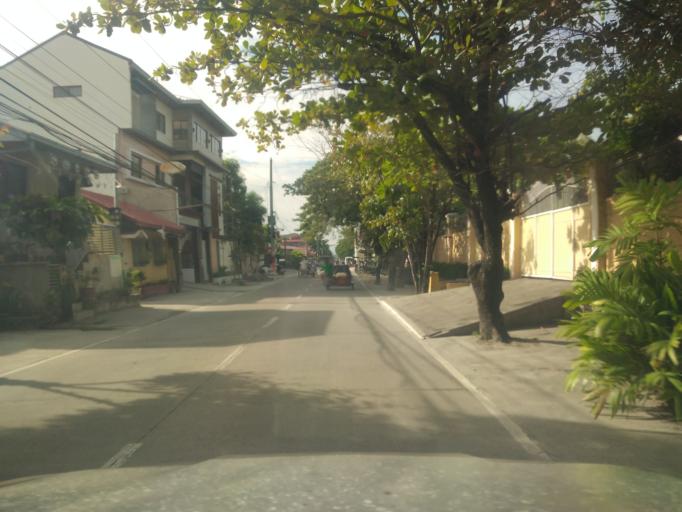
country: PH
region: Central Luzon
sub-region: Province of Pampanga
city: Sexmoan
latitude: 14.9494
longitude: 120.6240
